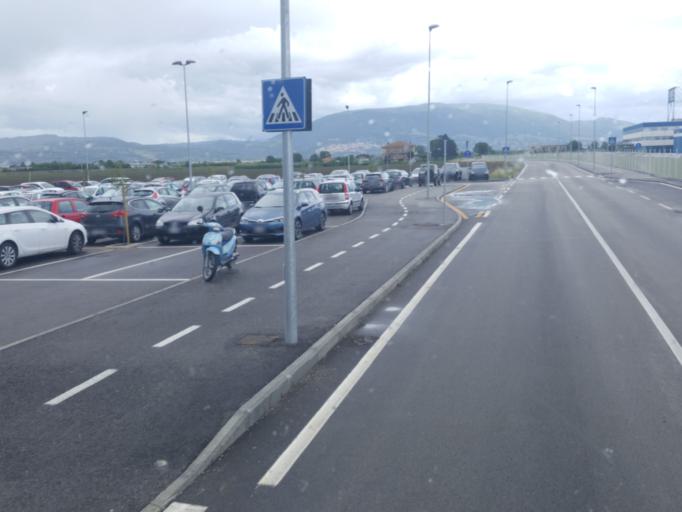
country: IT
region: Umbria
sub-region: Provincia di Perugia
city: Ospedalicchio
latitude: 43.0714
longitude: 12.5020
